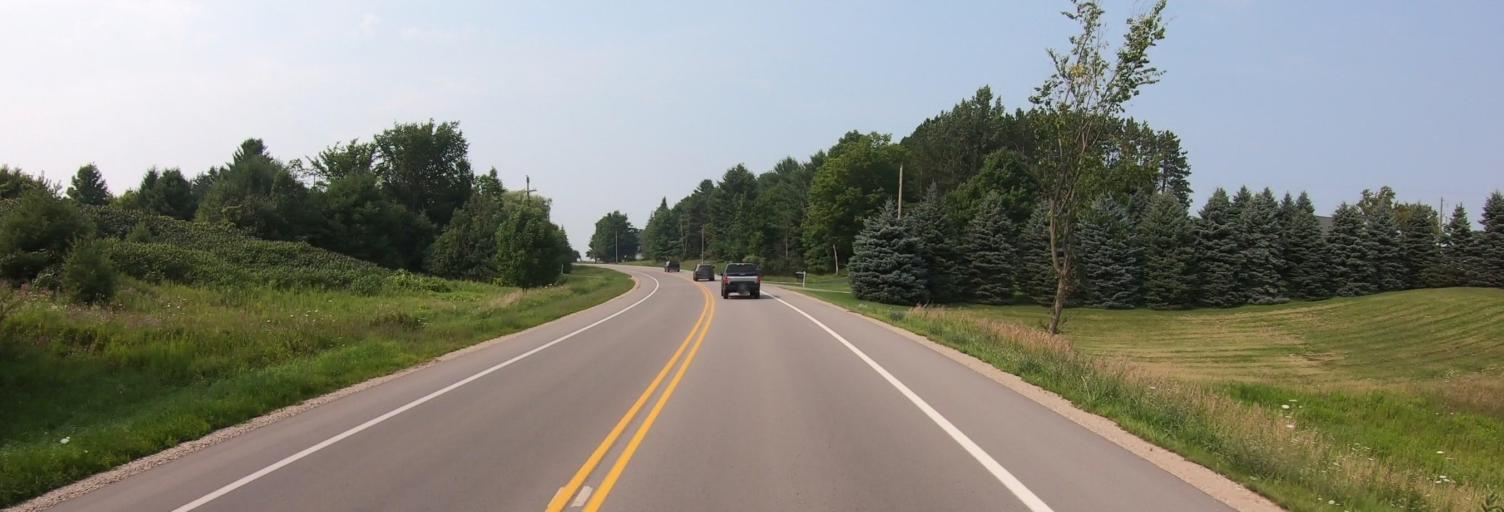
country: US
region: Michigan
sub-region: Charlevoix County
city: Charlevoix
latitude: 45.2547
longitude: -85.2612
